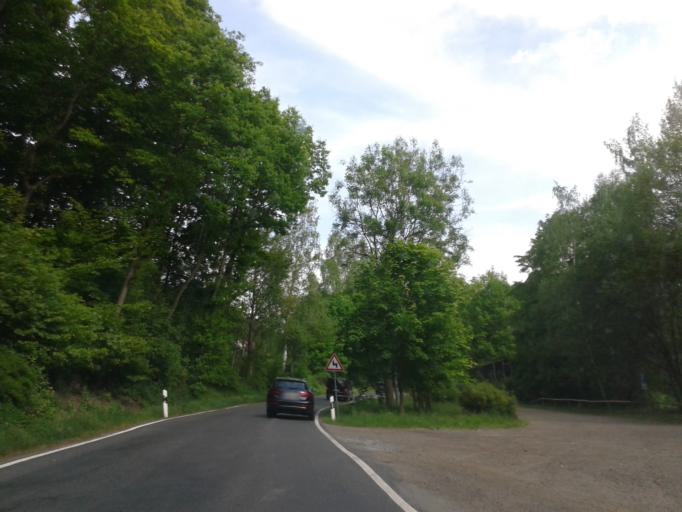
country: DE
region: Saxony
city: Reinsberg
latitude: 51.0108
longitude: 13.3489
